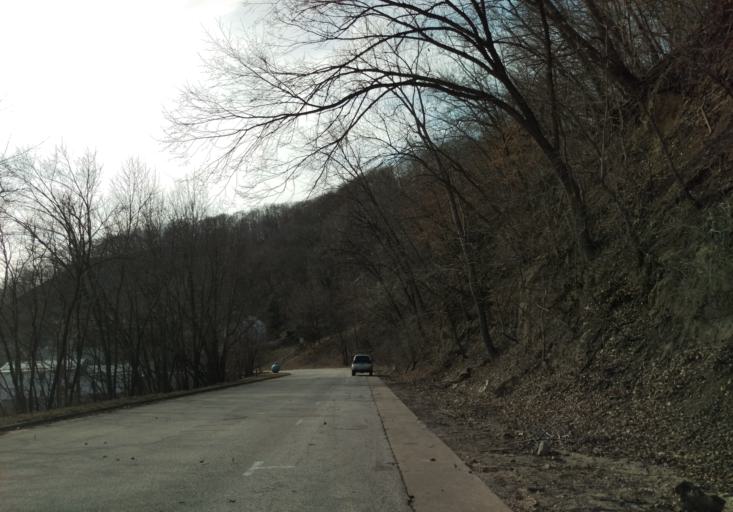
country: US
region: Wisconsin
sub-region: Crawford County
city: Prairie du Chien
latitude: 43.0456
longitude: -91.1785
